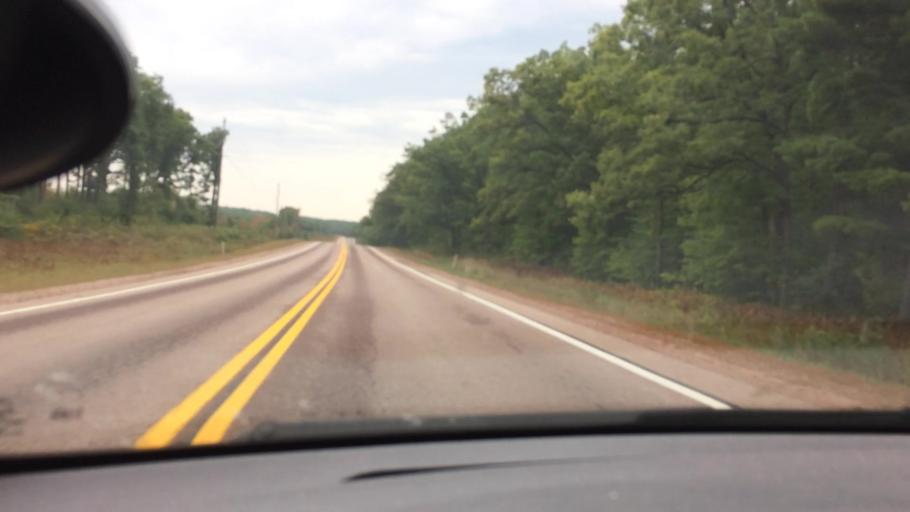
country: US
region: Wisconsin
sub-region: Clark County
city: Neillsville
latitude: 44.5862
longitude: -90.7500
